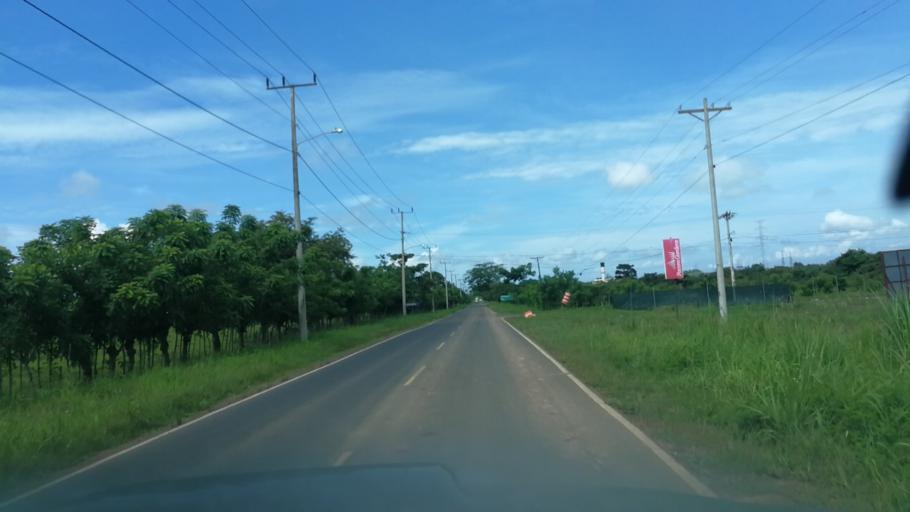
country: PA
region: Panama
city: Paso Blanco
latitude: 9.1100
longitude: -79.2665
